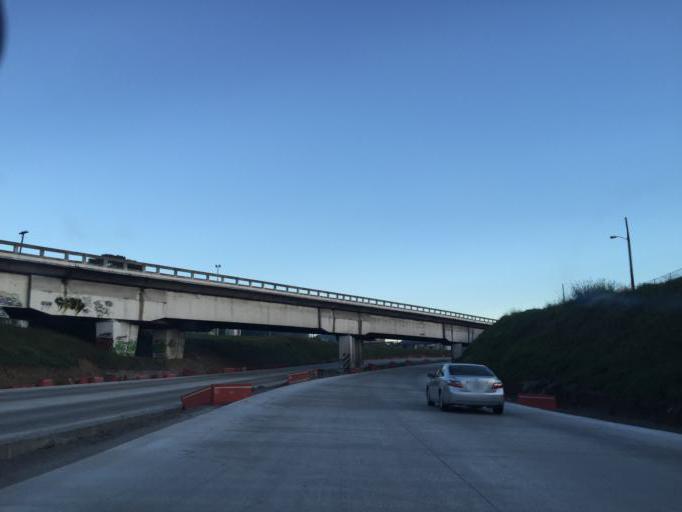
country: MX
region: Veracruz
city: Ixtac Zoquitlan
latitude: 18.8641
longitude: -97.0689
